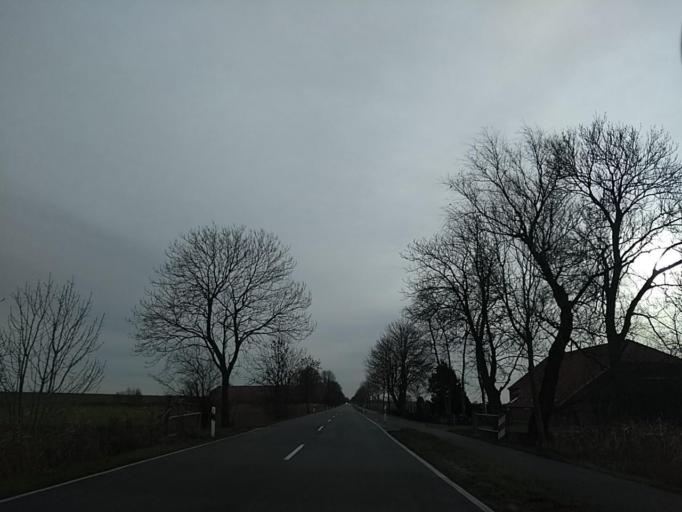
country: DE
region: Lower Saxony
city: Jemgum
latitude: 53.3056
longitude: 7.3380
